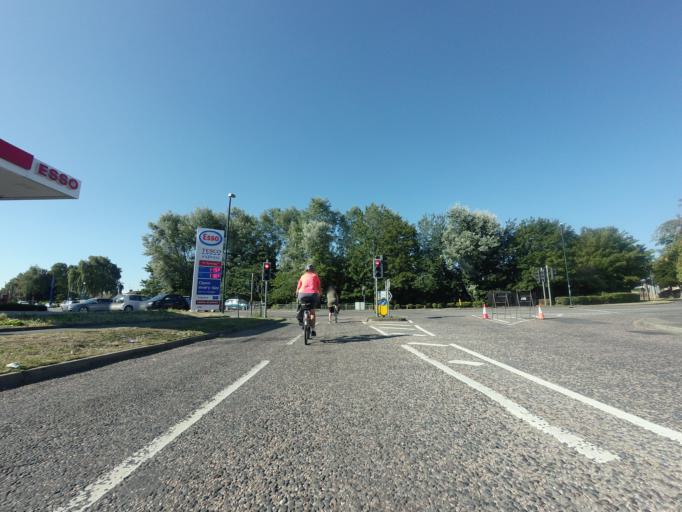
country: GB
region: England
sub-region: Kent
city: Strood
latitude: 51.4027
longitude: 0.4800
